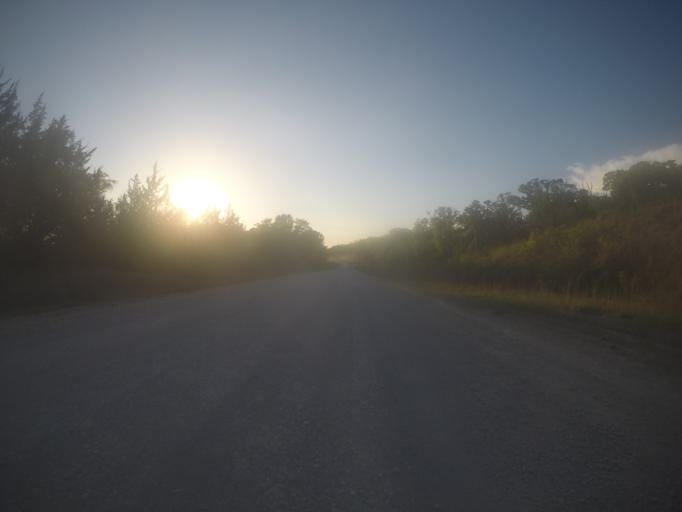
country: US
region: Kansas
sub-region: Riley County
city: Manhattan
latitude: 39.2399
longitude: -96.5590
